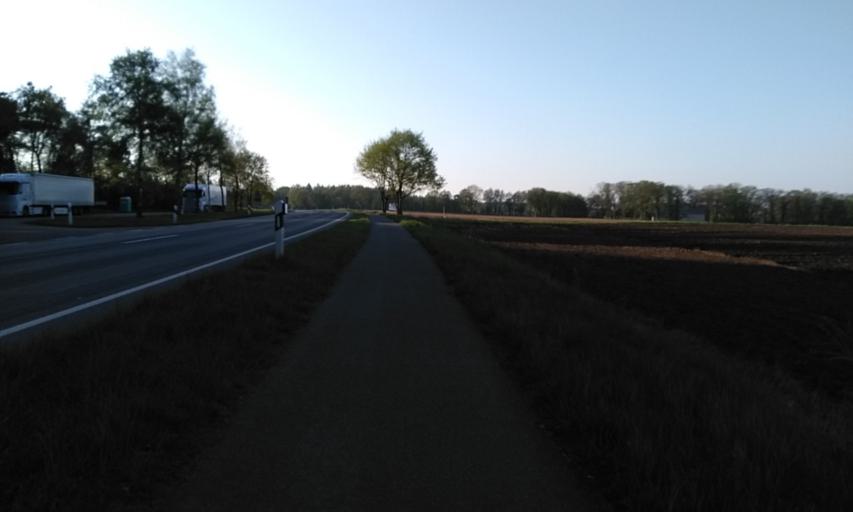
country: DE
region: Lower Saxony
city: Dollern
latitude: 53.5285
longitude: 9.5563
